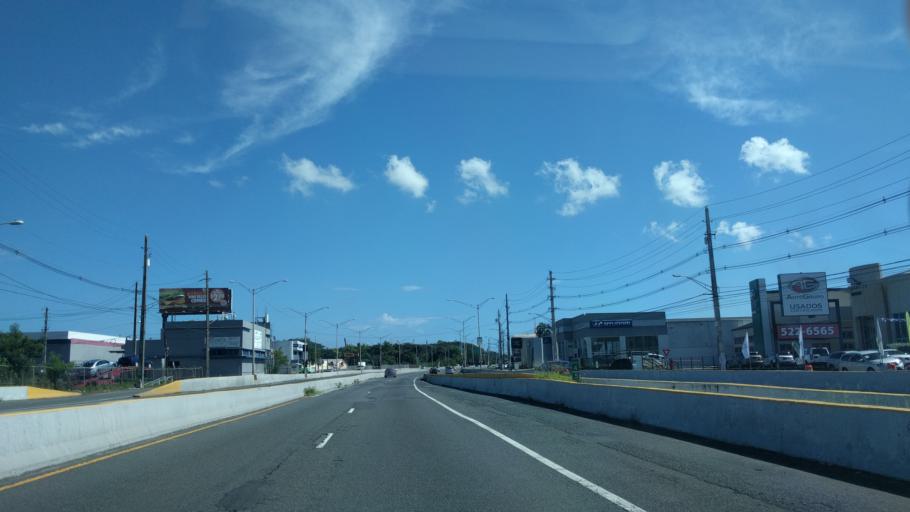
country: PR
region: Catano
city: Catano
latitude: 18.4206
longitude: -66.0987
